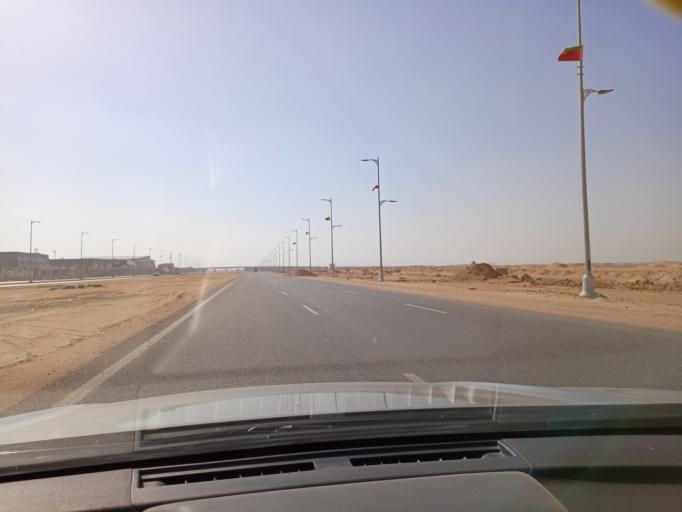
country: EG
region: Muhafazat al Qalyubiyah
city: Al Khankah
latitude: 30.0444
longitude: 31.6983
